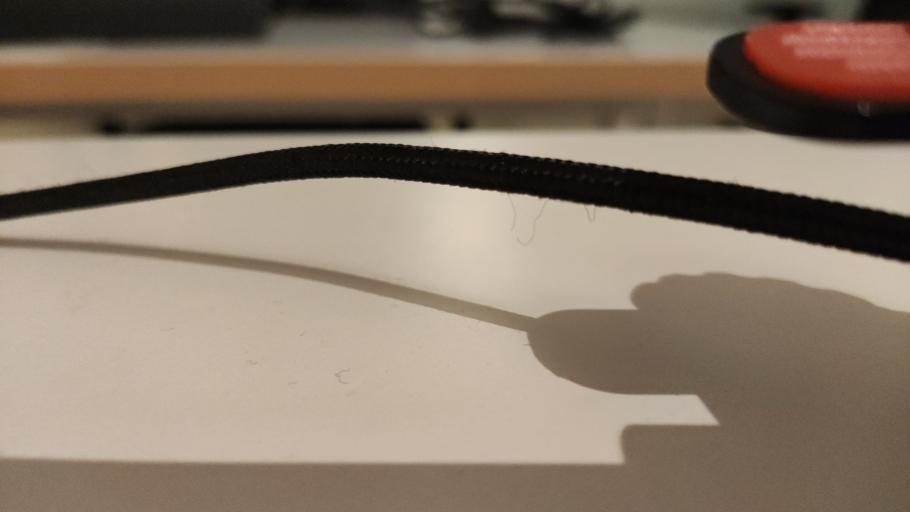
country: RU
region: Moskovskaya
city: Kurovskoye
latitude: 55.5936
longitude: 38.9233
